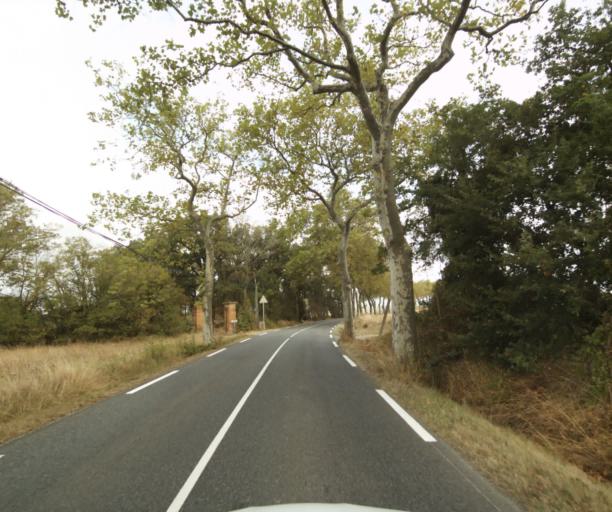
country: FR
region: Midi-Pyrenees
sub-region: Departement de la Haute-Garonne
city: Villefranche-de-Lauragais
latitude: 43.4129
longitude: 1.7158
